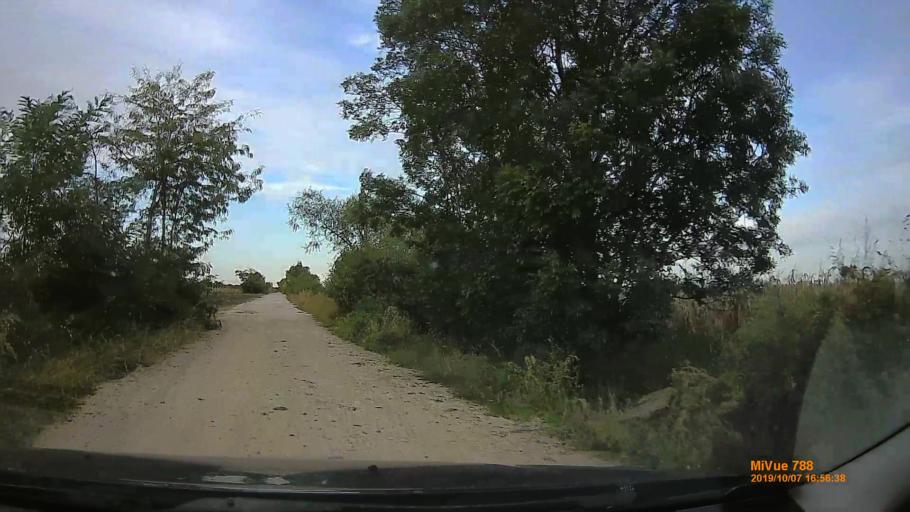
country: HU
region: Bekes
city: Szarvas
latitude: 46.8203
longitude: 20.5778
